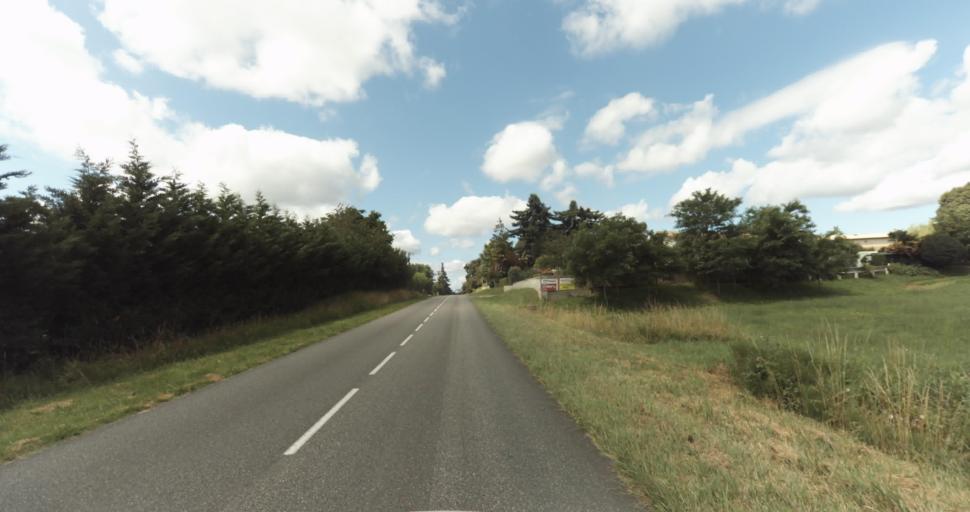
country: FR
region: Aquitaine
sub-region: Departement de la Gironde
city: Bazas
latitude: 44.4396
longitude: -0.2014
